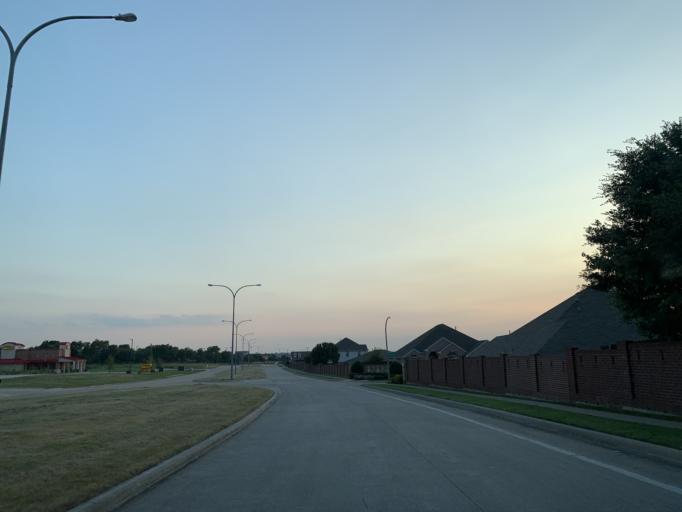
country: US
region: Texas
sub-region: Tarrant County
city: Keller
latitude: 32.9554
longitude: -97.2757
